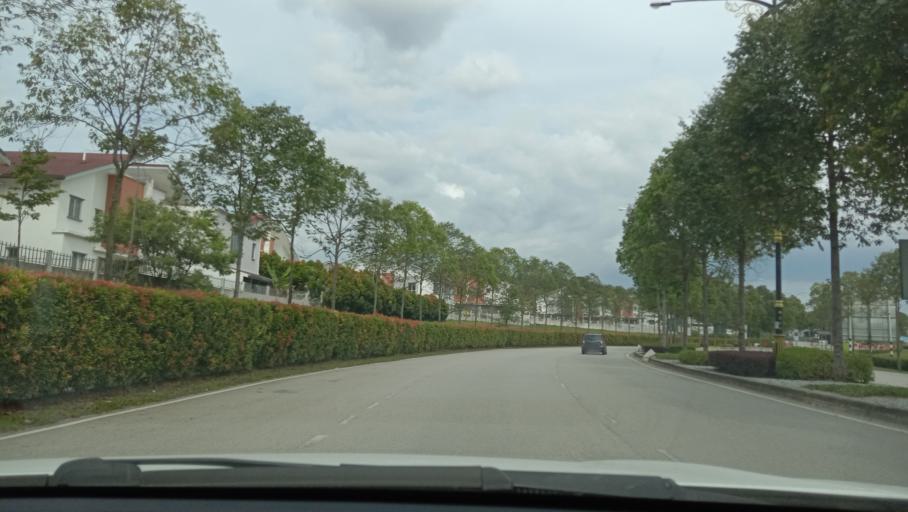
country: MY
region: Selangor
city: Ladang Seri Kundang
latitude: 3.2473
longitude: 101.4729
